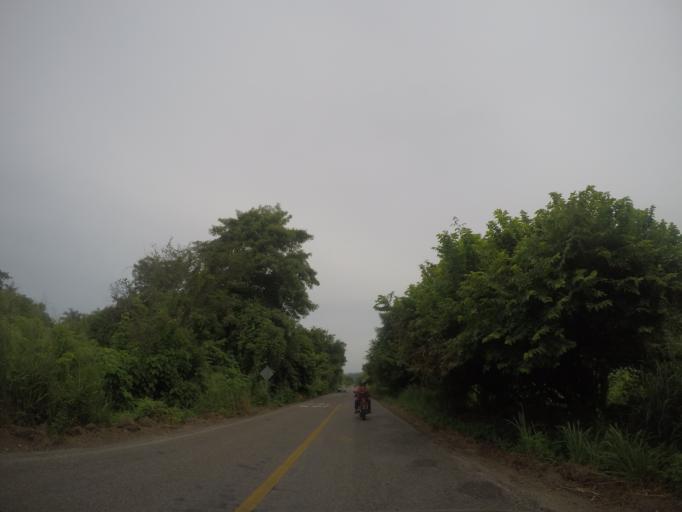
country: MX
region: Oaxaca
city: San Pedro Mixtepec
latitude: 15.9340
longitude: -97.1526
